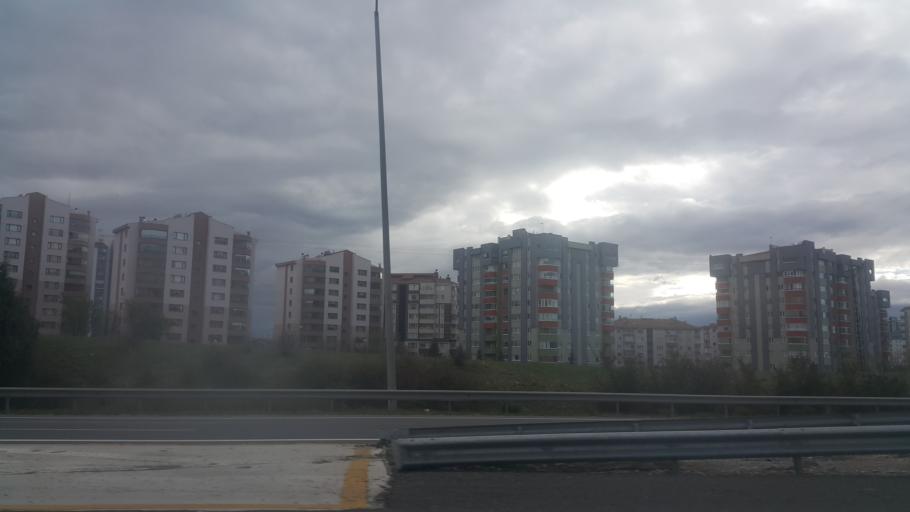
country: TR
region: Ankara
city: Etimesgut
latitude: 39.9991
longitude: 32.6364
